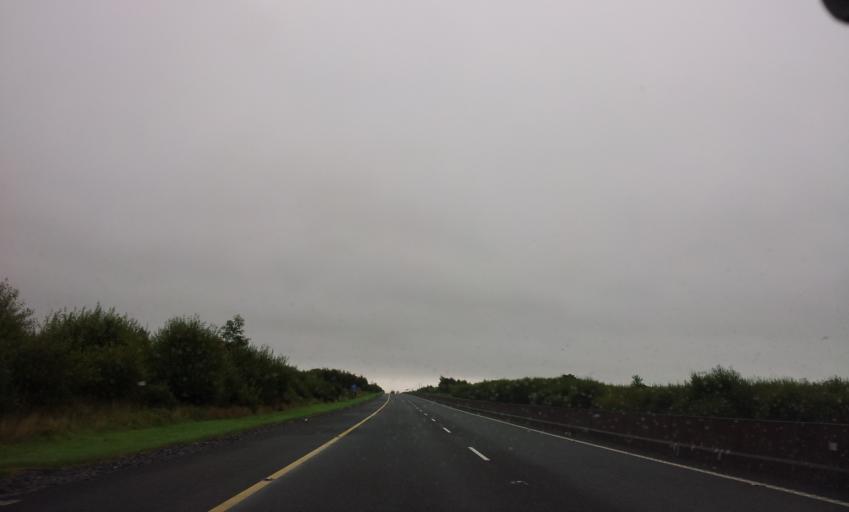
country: IE
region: Munster
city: Cahir
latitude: 52.3252
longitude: -8.0752
